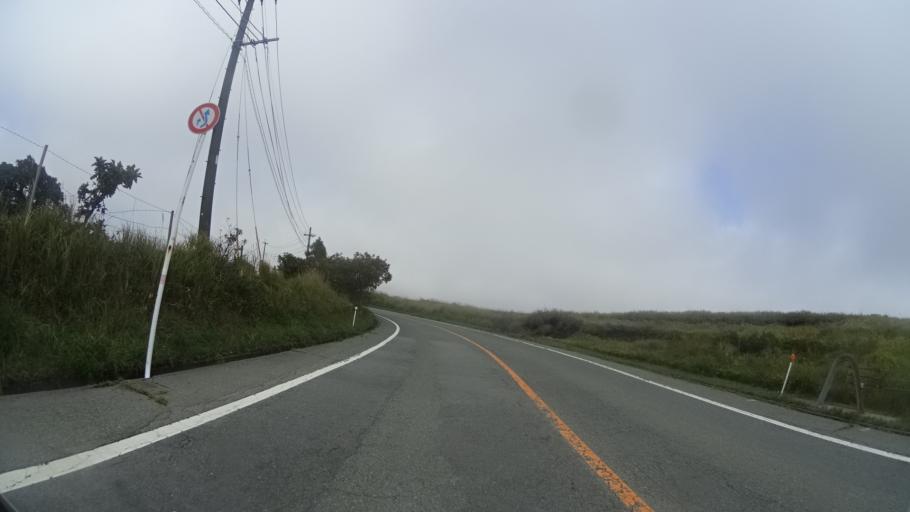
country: JP
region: Kumamoto
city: Aso
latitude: 32.9686
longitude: 131.0027
